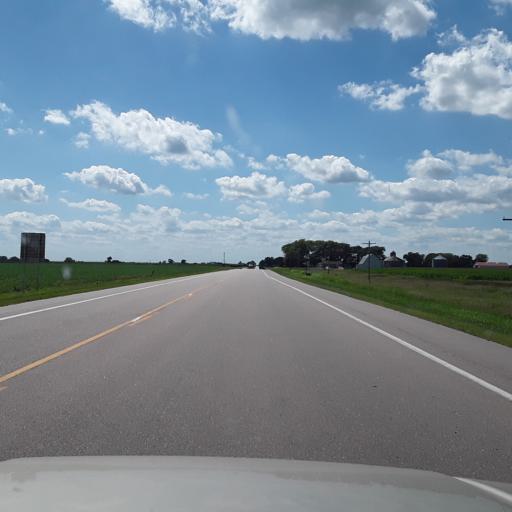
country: US
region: Nebraska
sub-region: Merrick County
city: Central City
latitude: 41.1910
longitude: -97.9858
